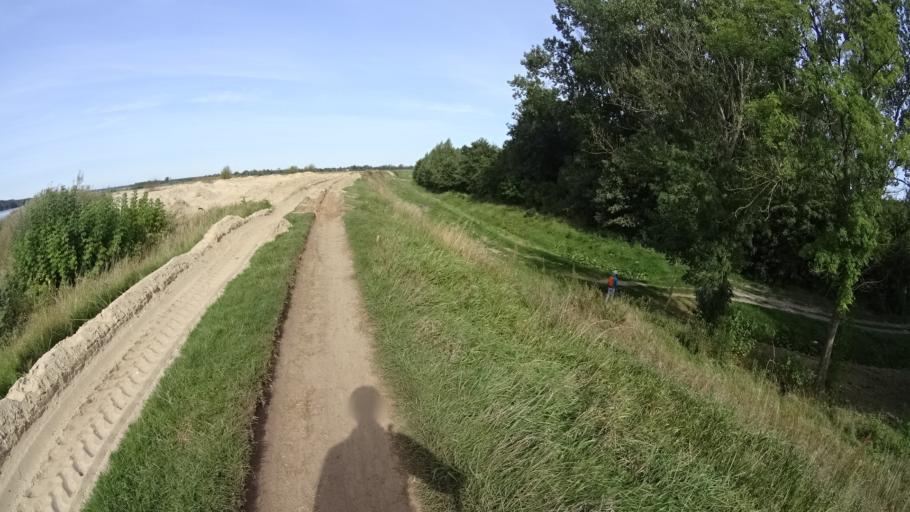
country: PL
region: Masovian Voivodeship
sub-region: Powiat legionowski
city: Serock
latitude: 52.5004
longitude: 21.0825
